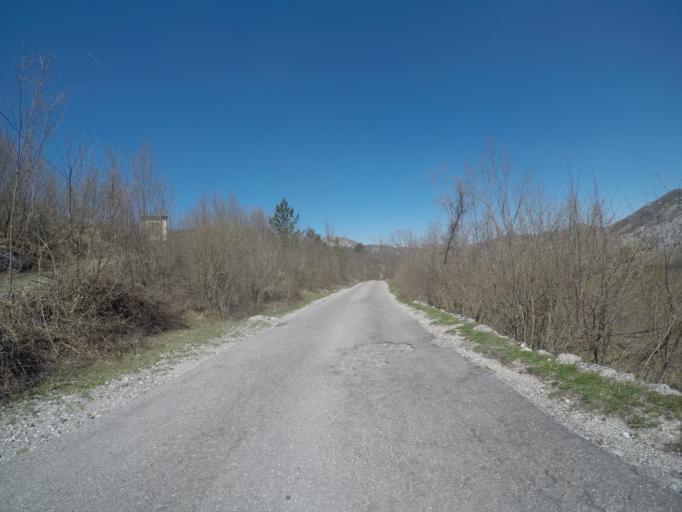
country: ME
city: Dobrota
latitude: 42.4676
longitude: 18.8566
